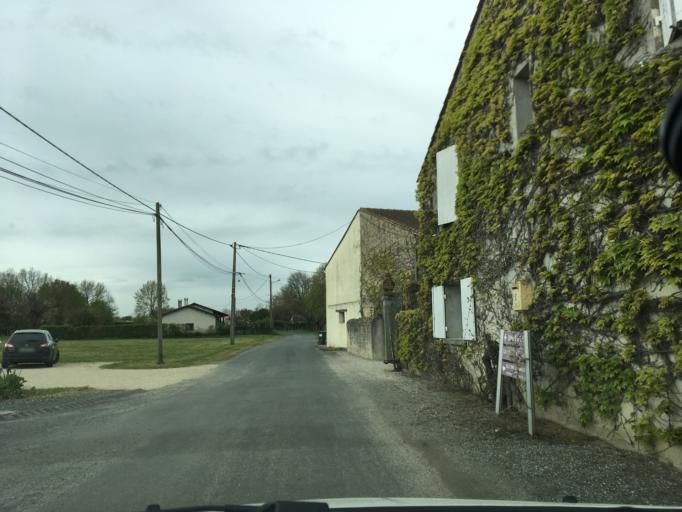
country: FR
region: Aquitaine
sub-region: Departement de la Gironde
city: Lesparre-Medoc
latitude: 45.3123
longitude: -0.8925
